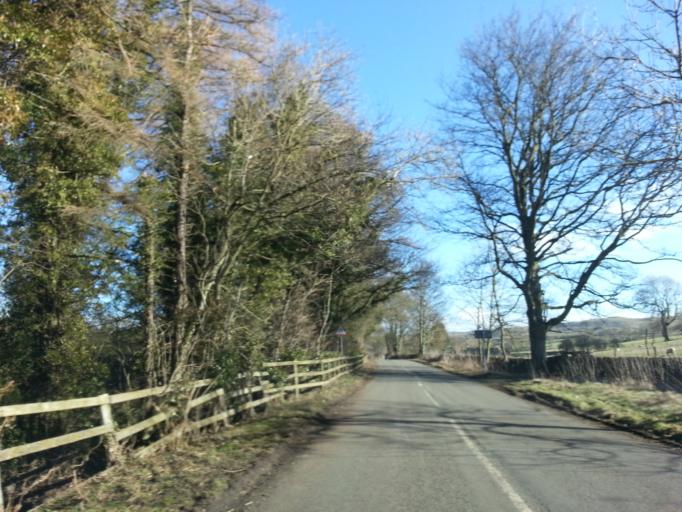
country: GB
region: England
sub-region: County Durham
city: Stanhope
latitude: 54.7268
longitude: -1.9745
